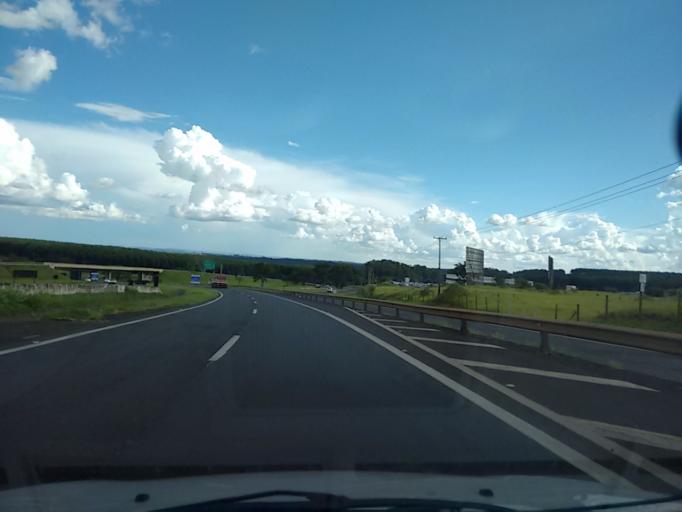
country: BR
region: Sao Paulo
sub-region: Sao Carlos
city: Sao Carlos
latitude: -22.0427
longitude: -47.8622
